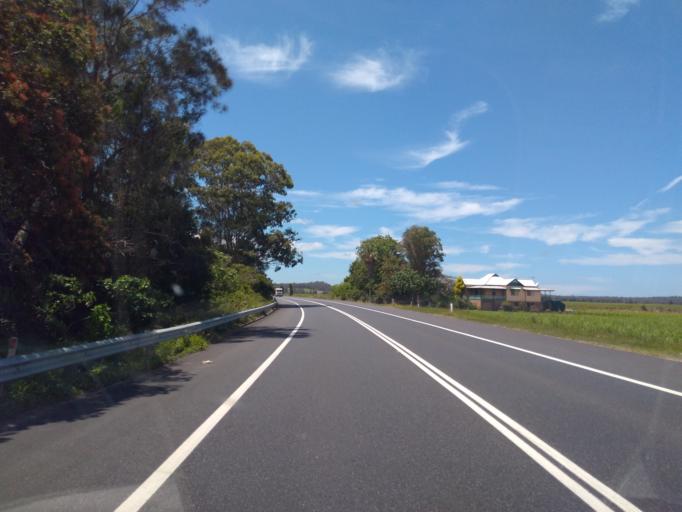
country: AU
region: New South Wales
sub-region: Clarence Valley
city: Maclean
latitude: -29.5352
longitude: 153.1856
